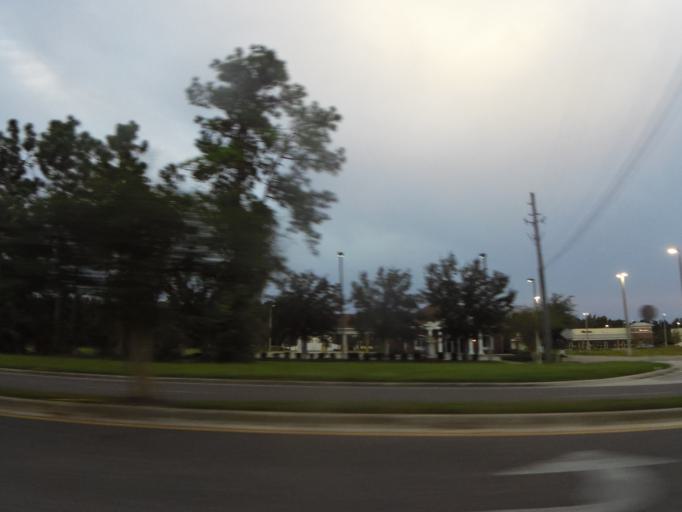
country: US
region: Florida
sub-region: Saint Johns County
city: Fruit Cove
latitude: 30.1140
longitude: -81.5881
